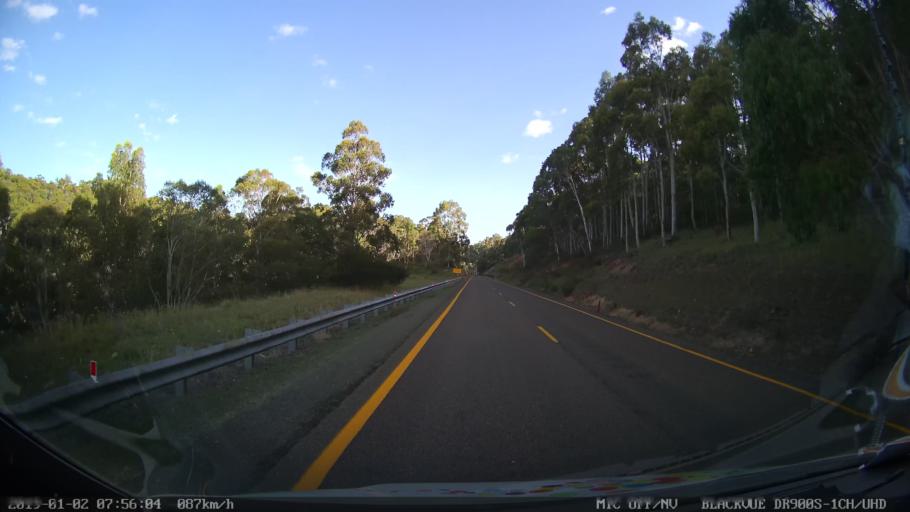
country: AU
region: New South Wales
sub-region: Tumut Shire
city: Tumut
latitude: -35.6753
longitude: 148.4860
